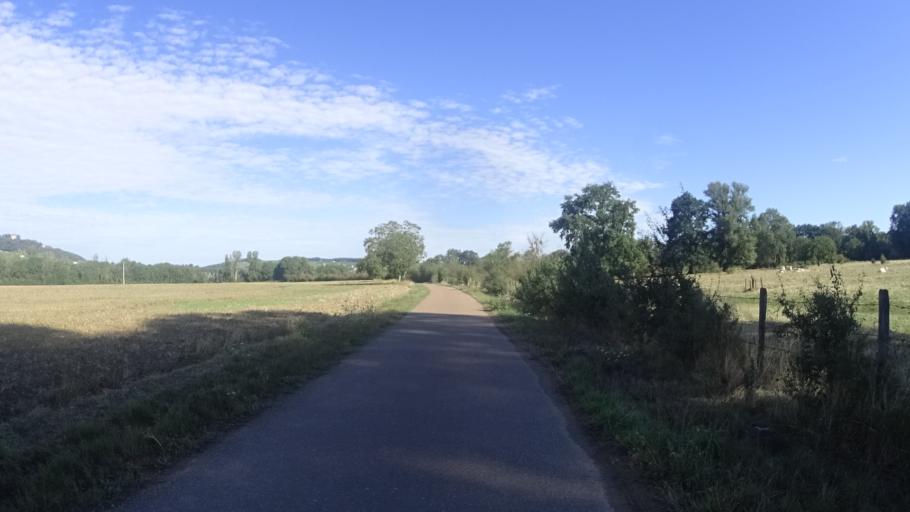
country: FR
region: Centre
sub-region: Departement du Cher
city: Sancerre
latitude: 47.3234
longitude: 2.8671
